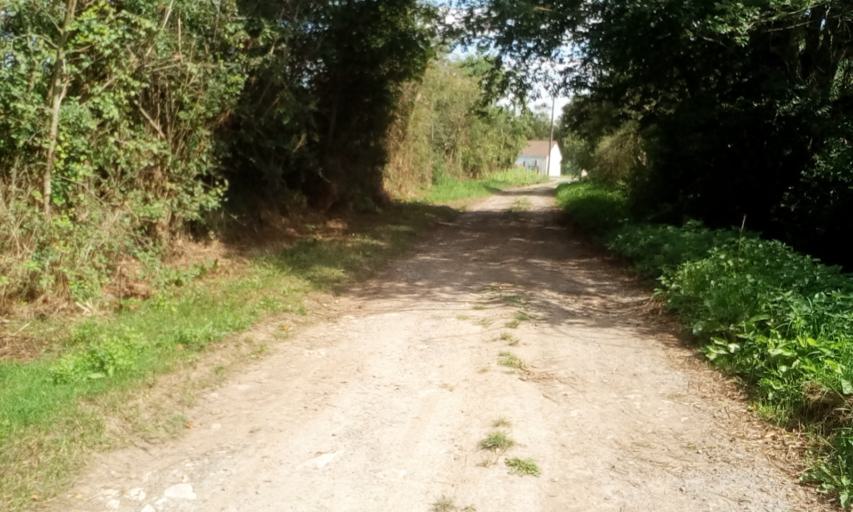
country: FR
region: Lower Normandy
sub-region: Departement du Calvados
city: Argences
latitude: 49.1451
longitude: -0.1498
